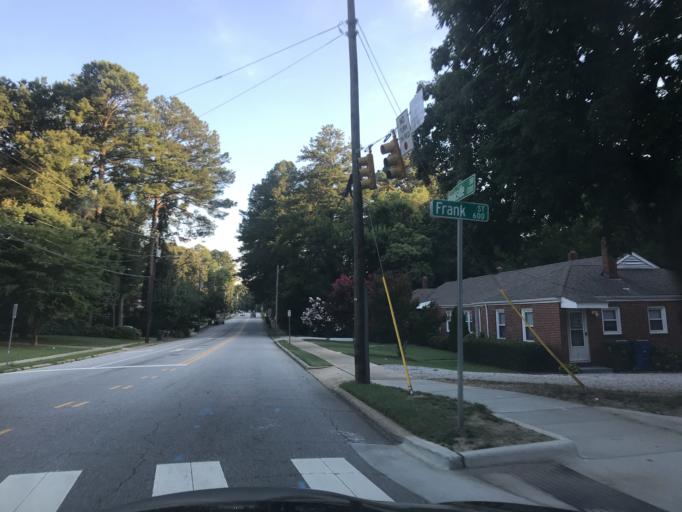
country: US
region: North Carolina
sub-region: Wake County
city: Raleigh
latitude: 35.7962
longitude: -78.6243
